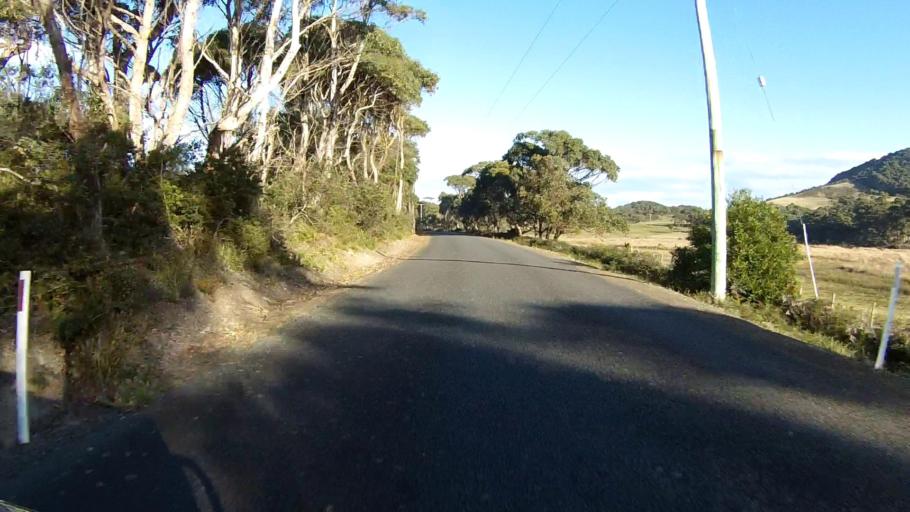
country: AU
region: Tasmania
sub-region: Clarence
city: Sandford
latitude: -43.1786
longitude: 147.8527
